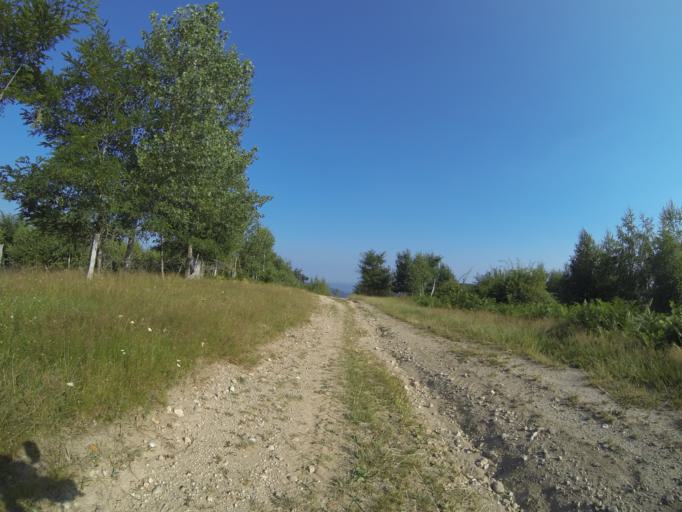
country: RO
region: Valcea
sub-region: Comuna Vaideeni
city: Vaideeni
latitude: 45.2009
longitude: 23.9798
